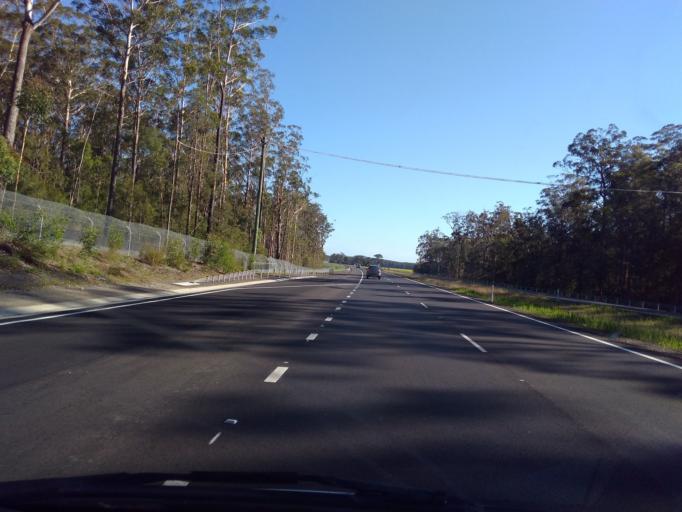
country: AU
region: New South Wales
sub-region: Port Macquarie-Hastings
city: North Shore
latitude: -31.3598
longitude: 152.8049
